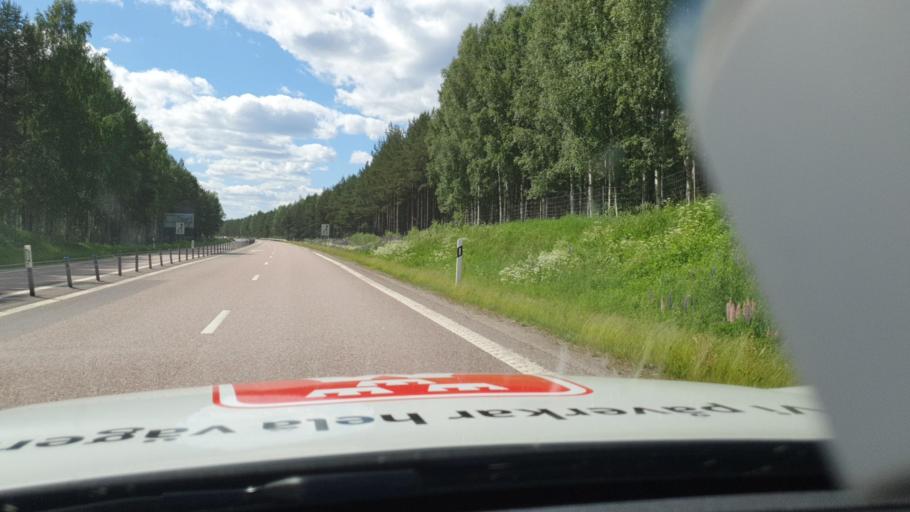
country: SE
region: Gaevleborg
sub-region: Sandvikens Kommun
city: Sandviken
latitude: 60.6294
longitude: 16.7758
